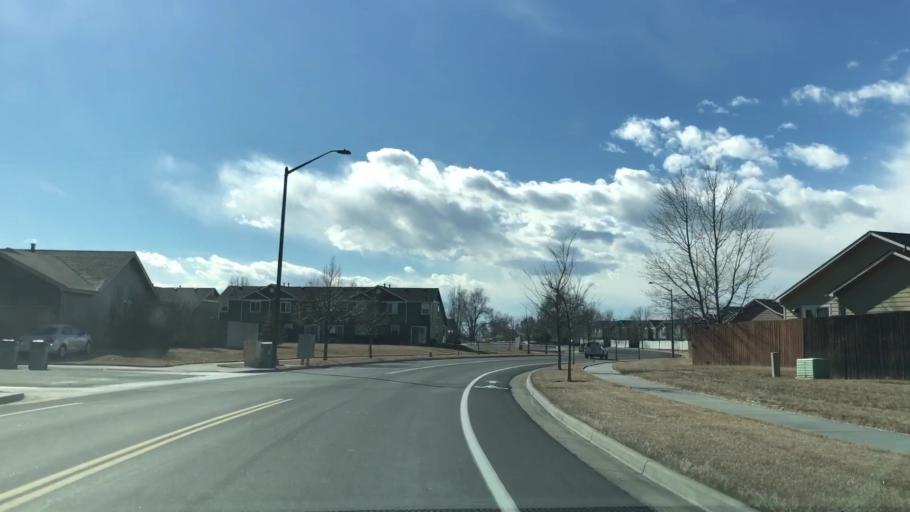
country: US
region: Colorado
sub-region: Larimer County
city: Fort Collins
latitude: 40.5983
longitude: -105.0039
